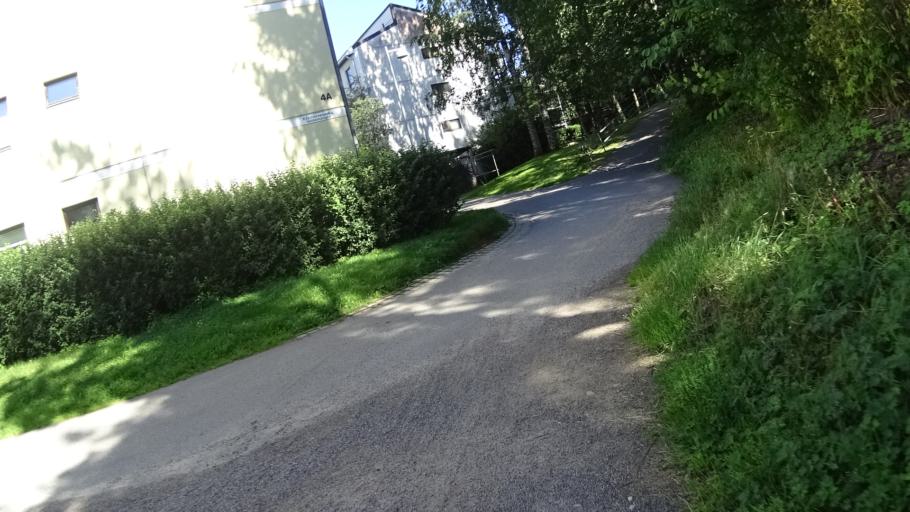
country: FI
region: Uusimaa
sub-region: Helsinki
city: Teekkarikylae
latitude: 60.2383
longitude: 24.8709
